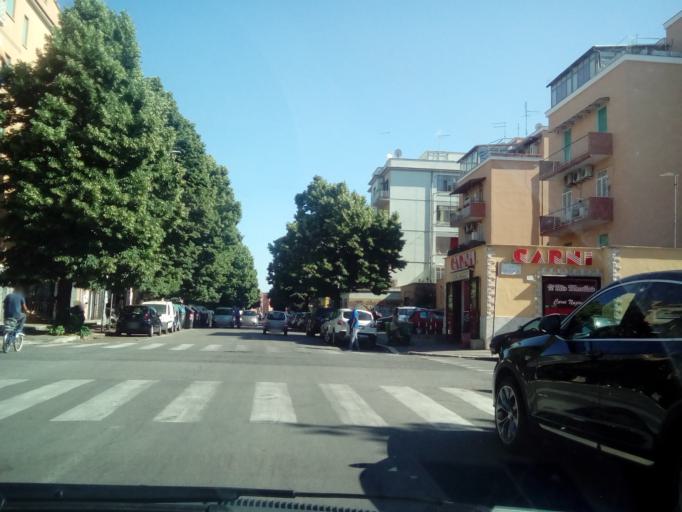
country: IT
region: Latium
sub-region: Citta metropolitana di Roma Capitale
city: Rome
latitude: 41.8908
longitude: 12.5665
